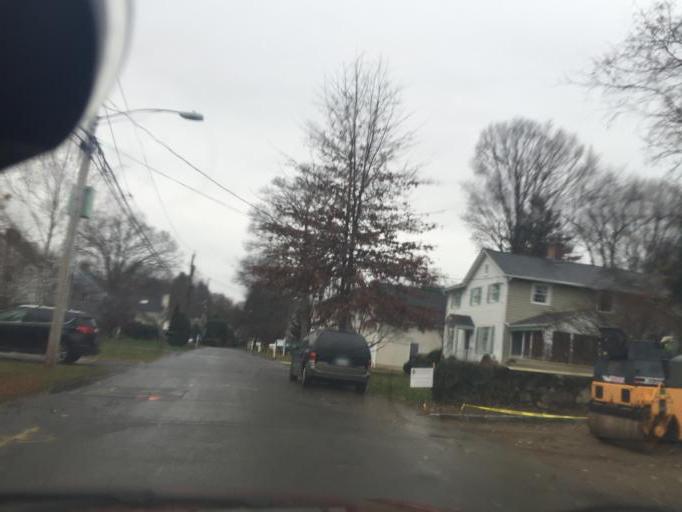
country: US
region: Connecticut
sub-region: Fairfield County
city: Southport
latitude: 41.1395
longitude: -73.2925
